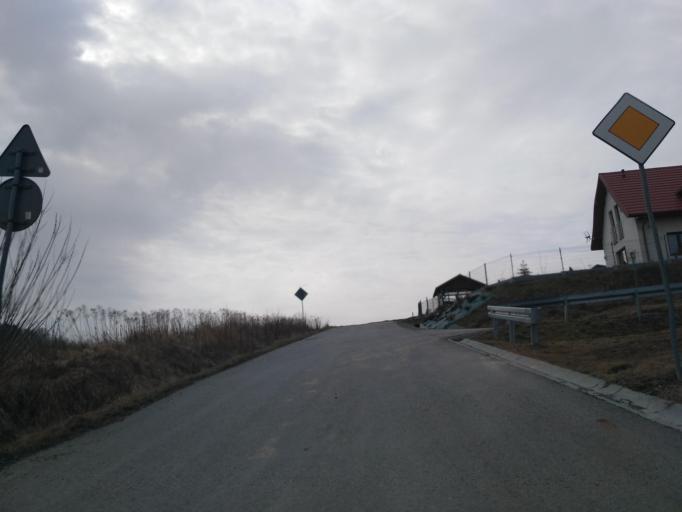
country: PL
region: Subcarpathian Voivodeship
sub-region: Powiat ropczycko-sedziszowski
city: Wielopole Skrzynskie
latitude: 49.9410
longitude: 21.6137
